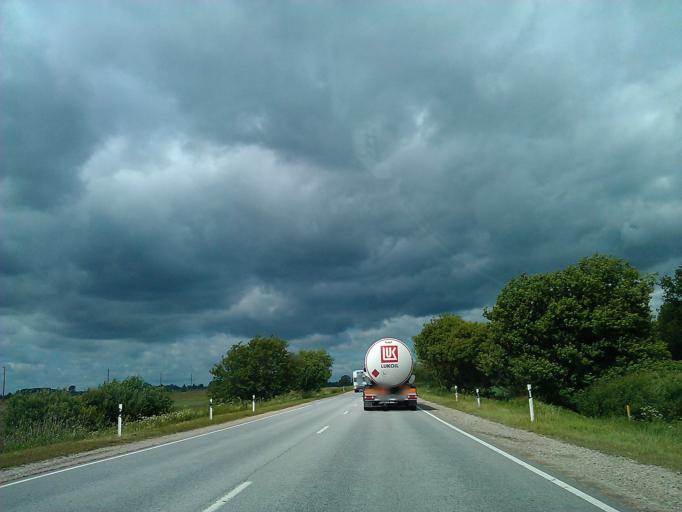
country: LV
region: Engure
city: Smarde
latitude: 56.9203
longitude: 23.2995
